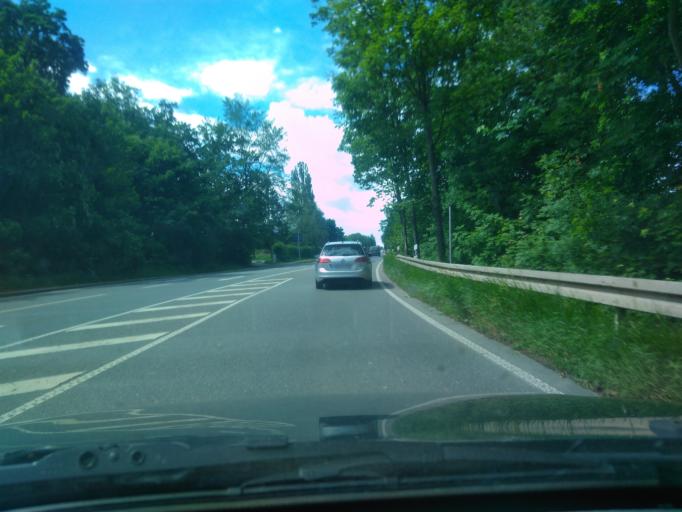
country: DE
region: Thuringia
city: Weimar
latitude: 50.9622
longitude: 11.3187
